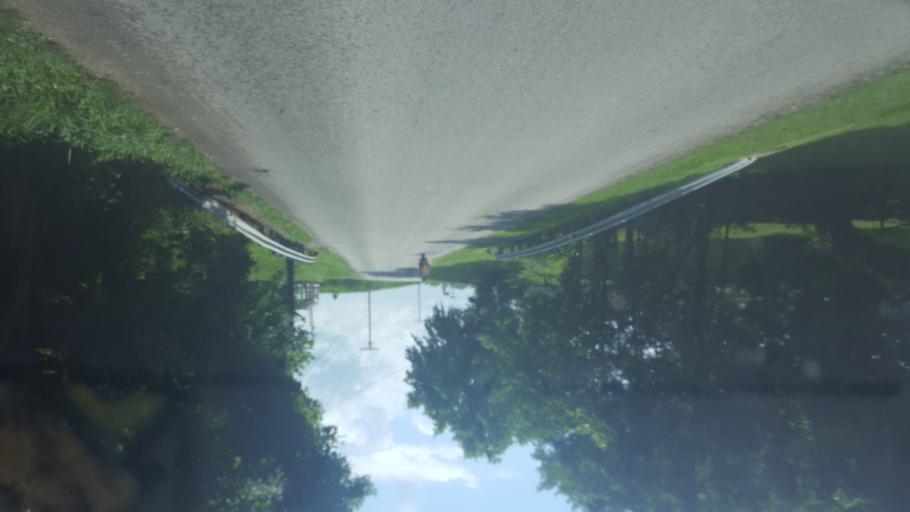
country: US
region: Ohio
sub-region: Ross County
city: Kingston
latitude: 39.5538
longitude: -82.7755
